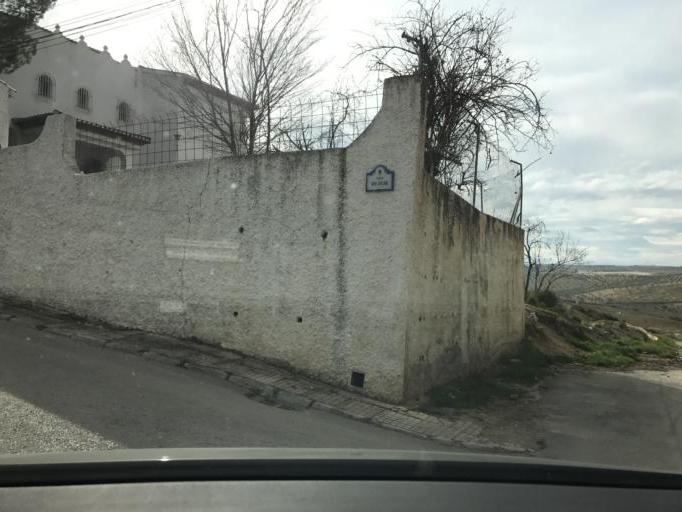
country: ES
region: Andalusia
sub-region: Provincia de Granada
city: Las Gabias
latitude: 37.1437
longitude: -3.6852
